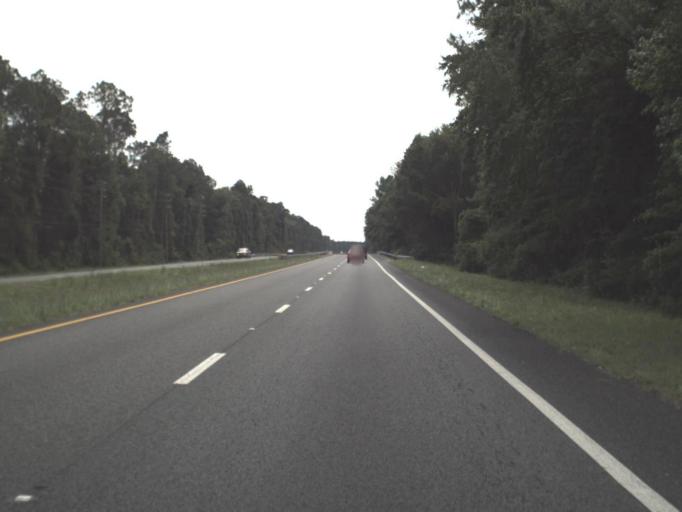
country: US
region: Florida
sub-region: Nassau County
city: Hilliard
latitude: 30.6406
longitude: -81.8650
